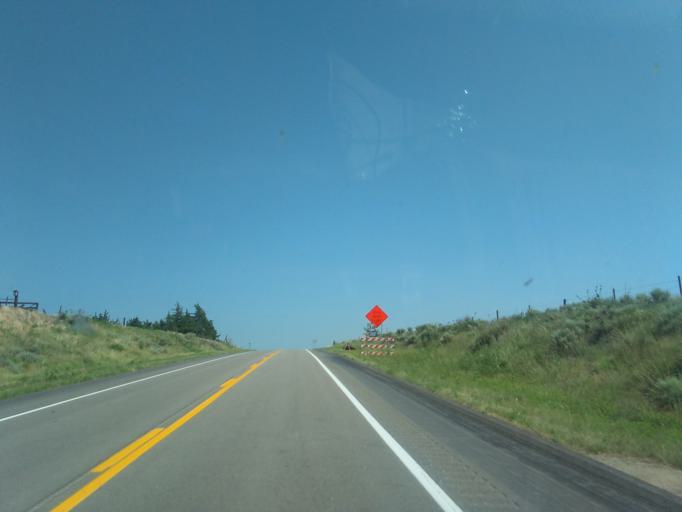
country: US
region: Nebraska
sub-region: Dundy County
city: Benkelman
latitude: 40.0161
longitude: -101.5426
